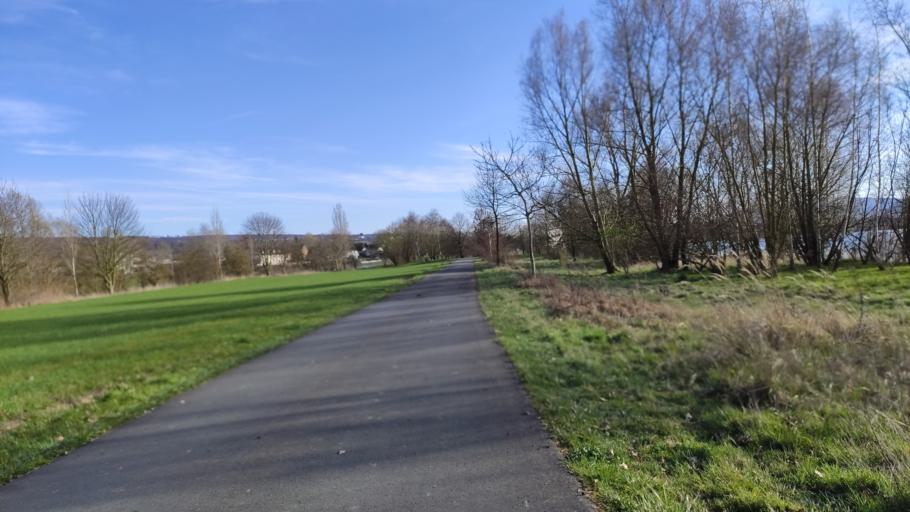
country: DE
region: Lower Saxony
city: Boffzen
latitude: 51.7560
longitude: 9.3834
